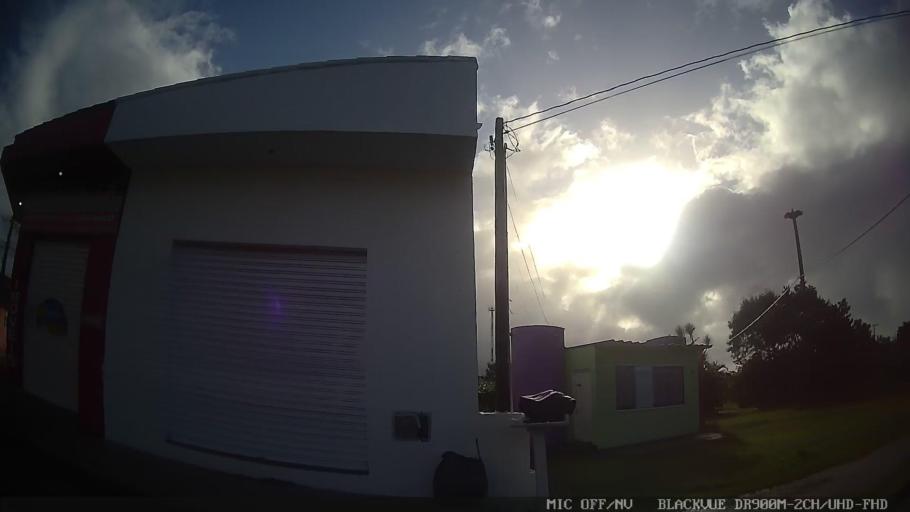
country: BR
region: Sao Paulo
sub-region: Itanhaem
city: Itanhaem
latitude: -24.2376
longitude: -46.8984
